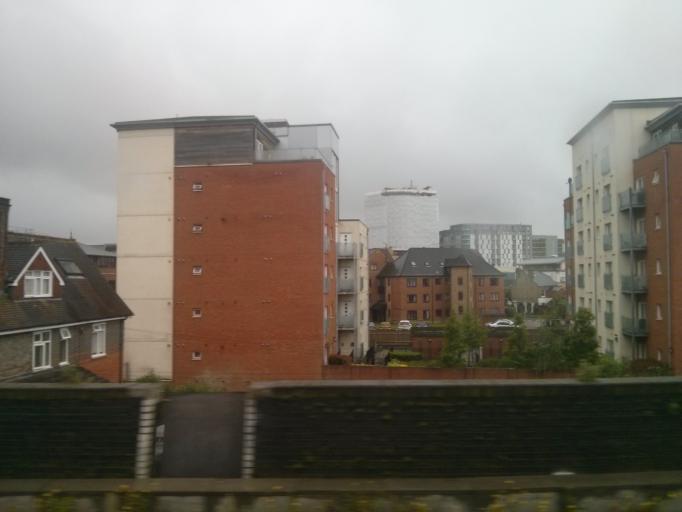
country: GB
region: England
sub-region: Reading
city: Reading
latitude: 51.4594
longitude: -0.9772
